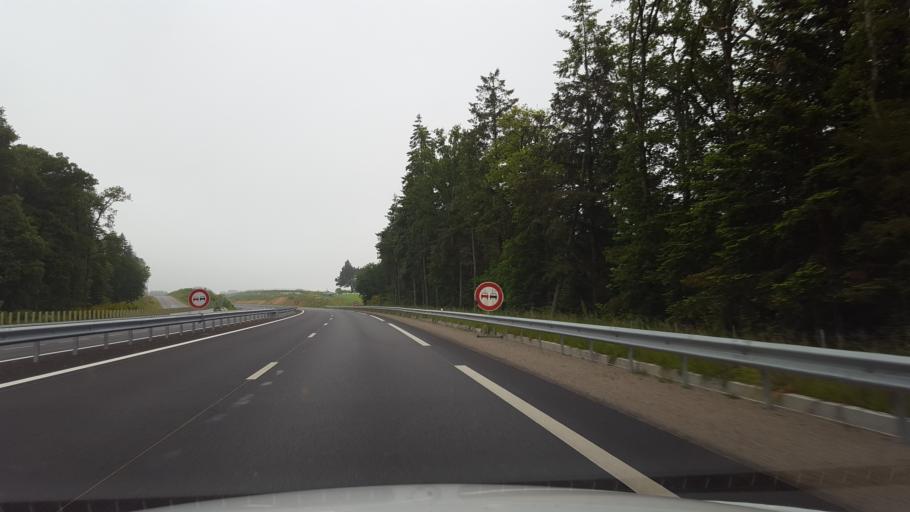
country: FR
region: Brittany
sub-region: Departement d'Ille-et-Vilaine
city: Guignen
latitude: 47.9167
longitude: -1.8580
